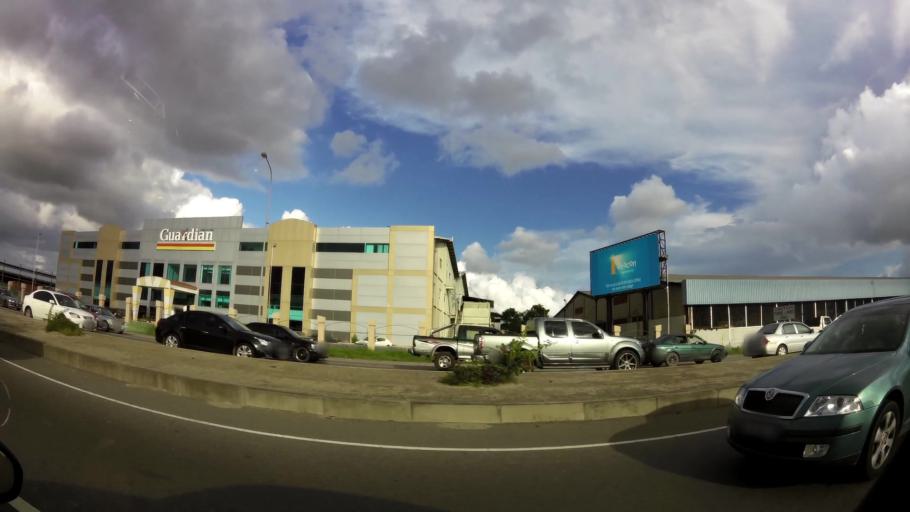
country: TT
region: Chaguanas
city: Chaguanas
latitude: 10.5215
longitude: -61.4086
